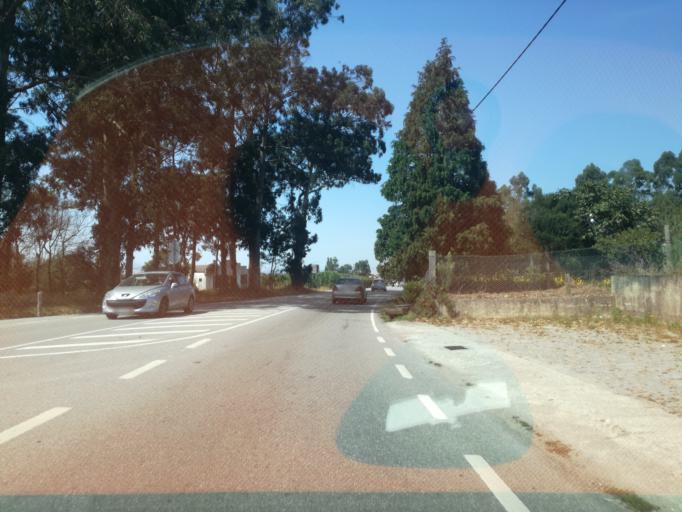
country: PT
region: Braga
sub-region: Esposende
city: Apulia
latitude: 41.4814
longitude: -8.7487
